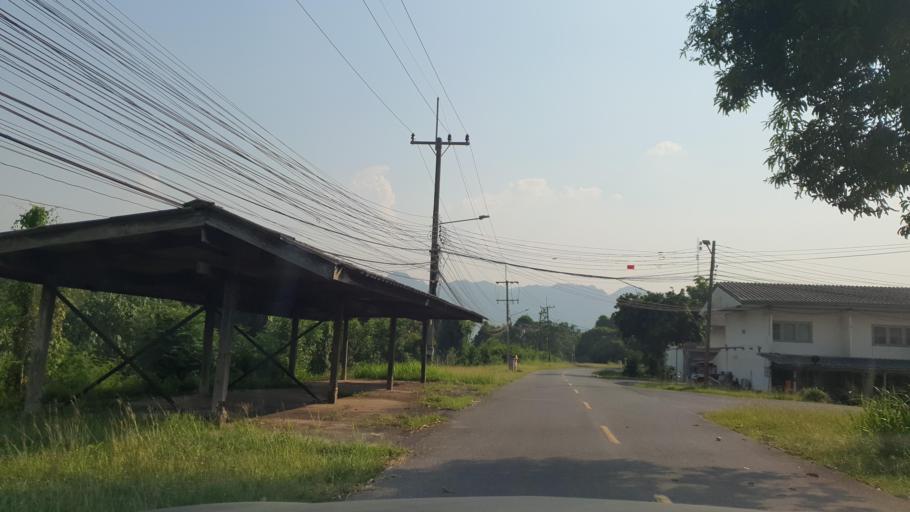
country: TH
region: Kanchanaburi
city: Sai Yok
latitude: 14.2263
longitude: 99.2340
